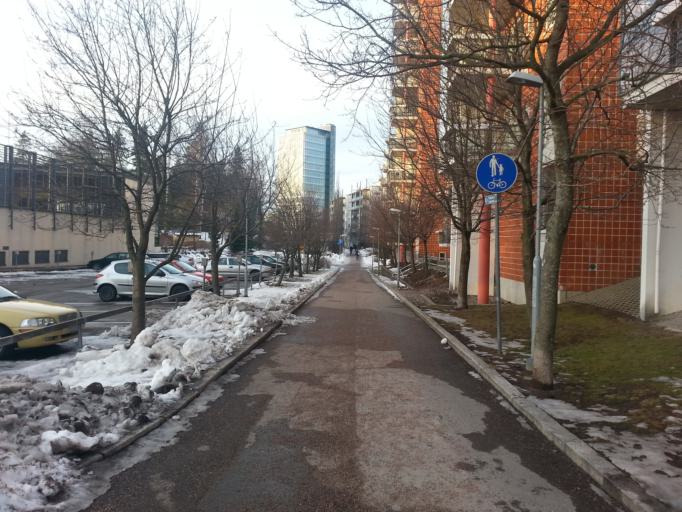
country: FI
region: Uusimaa
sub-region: Helsinki
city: Teekkarikylae
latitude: 60.2178
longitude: 24.8706
